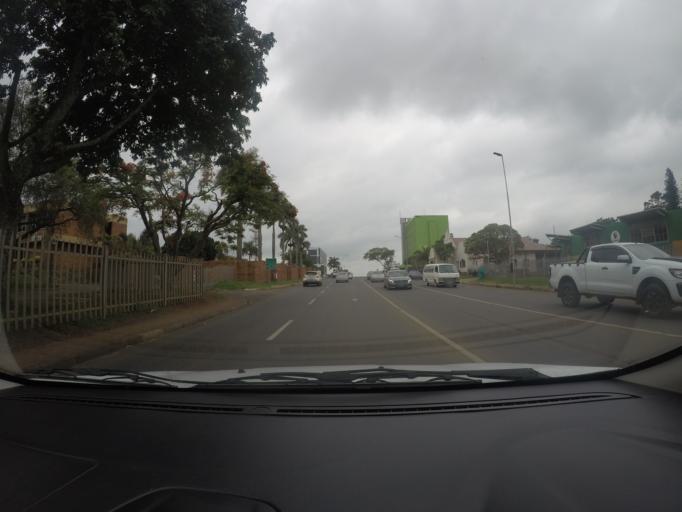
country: ZA
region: KwaZulu-Natal
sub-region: uThungulu District Municipality
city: Empangeni
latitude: -28.7456
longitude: 31.8909
